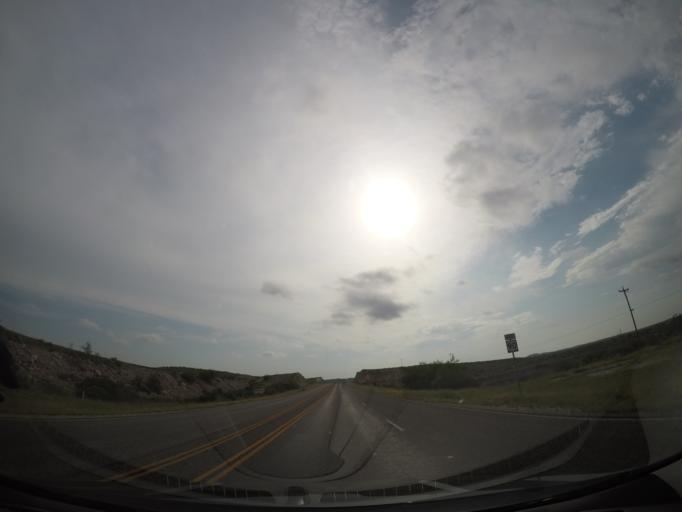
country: US
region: Texas
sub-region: Val Verde County
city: Cienegas Terrace
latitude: 29.8164
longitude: -101.5586
